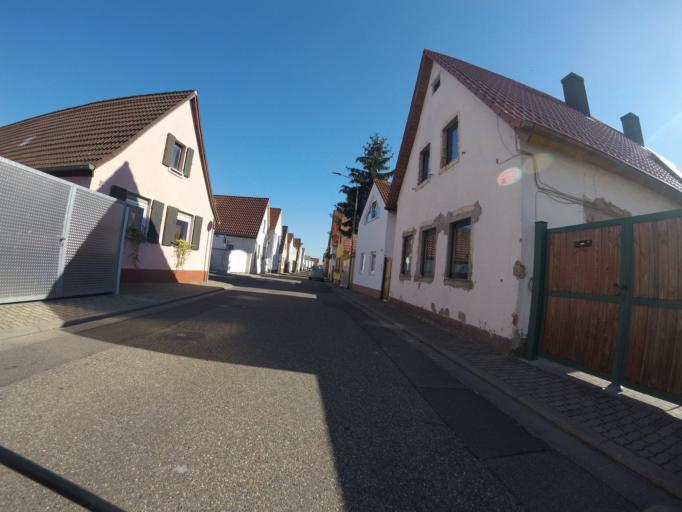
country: DE
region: Rheinland-Pfalz
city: Dudenhofen
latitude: 49.2644
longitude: 8.4033
